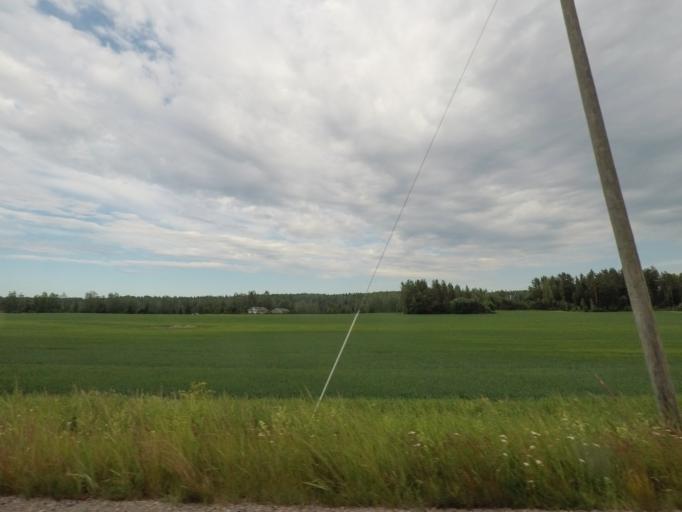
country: FI
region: Uusimaa
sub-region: Helsinki
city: Maentsaelae
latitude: 60.7530
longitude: 25.4327
